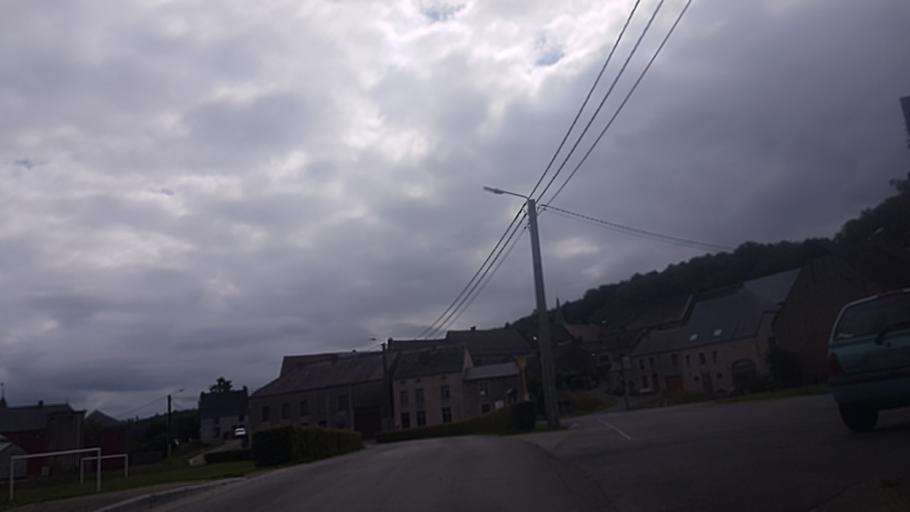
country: BE
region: Wallonia
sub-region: Province de Namur
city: Couvin
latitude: 50.1056
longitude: 4.5671
